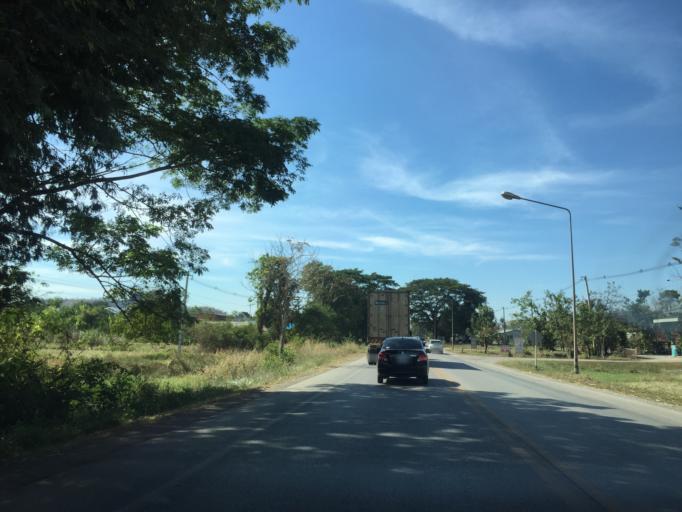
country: TH
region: Changwat Nong Bua Lamphu
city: Na Klang
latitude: 17.3223
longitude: 102.1398
